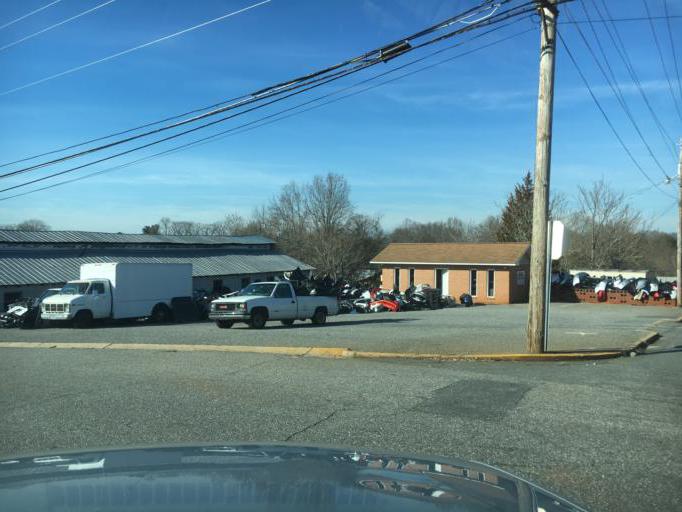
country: US
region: North Carolina
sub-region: Rutherford County
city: Forest City
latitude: 35.3346
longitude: -81.8619
